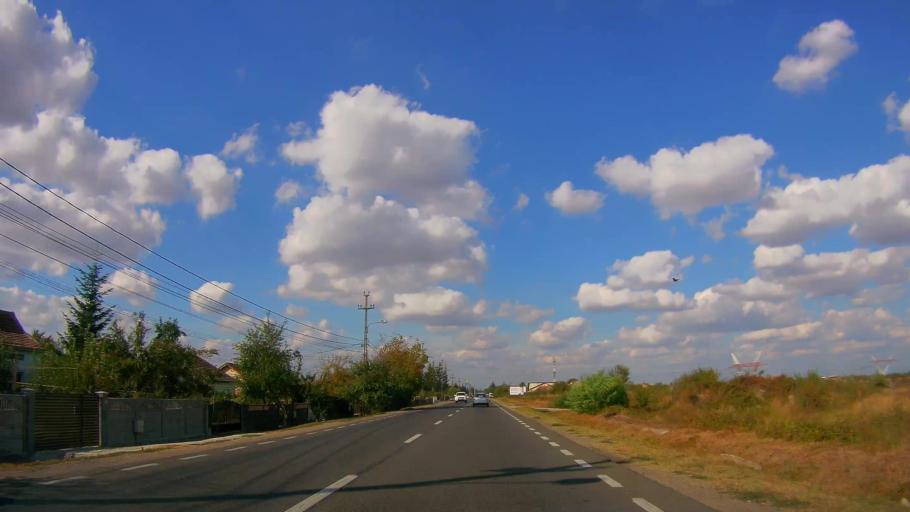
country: RO
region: Satu Mare
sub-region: Comuna Paulesti
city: Paulesti
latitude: 47.7578
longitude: 22.8833
